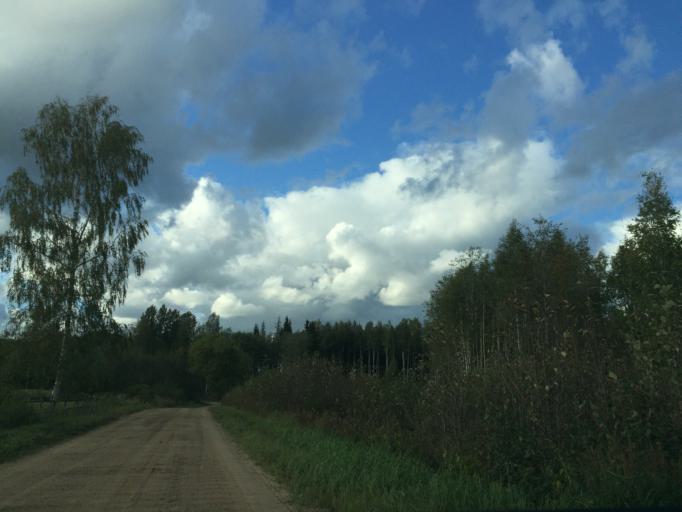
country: LV
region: Ligatne
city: Ligatne
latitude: 57.1338
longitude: 25.0994
